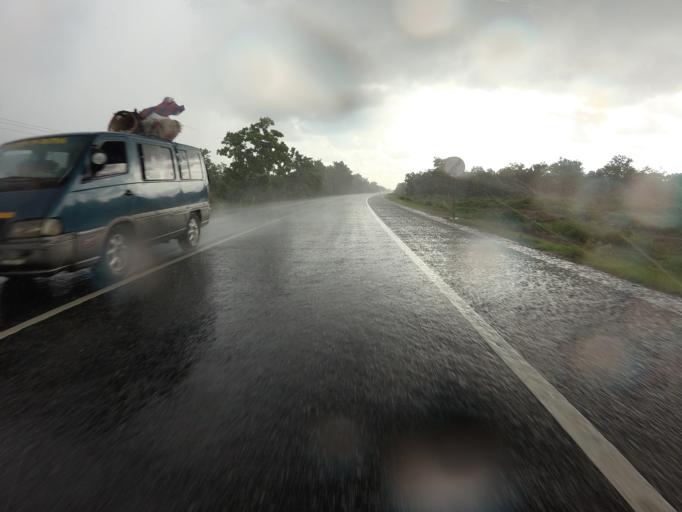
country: GH
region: Northern
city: Tamale
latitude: 9.1229
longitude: -1.6205
